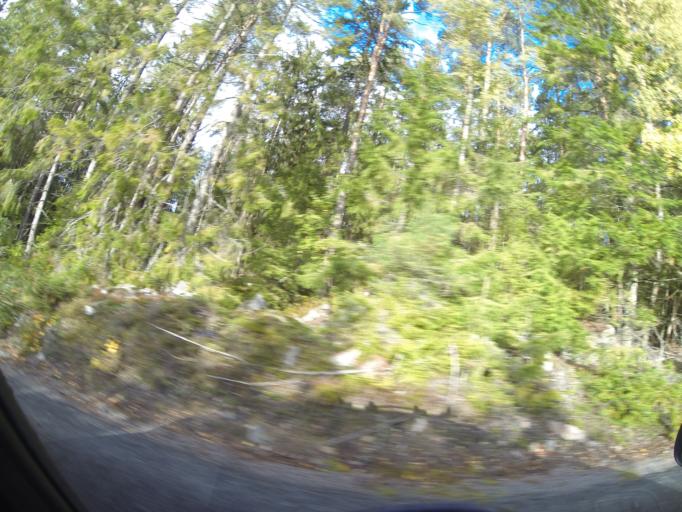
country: SE
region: Soedermanland
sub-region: Eskilstuna Kommun
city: Hallbybrunn
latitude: 59.3525
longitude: 16.3887
